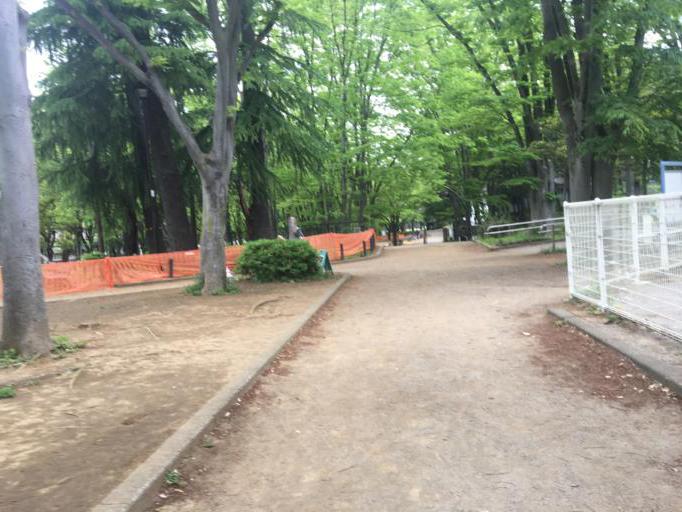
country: JP
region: Saitama
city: Shimotoda
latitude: 35.7561
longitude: 139.6718
